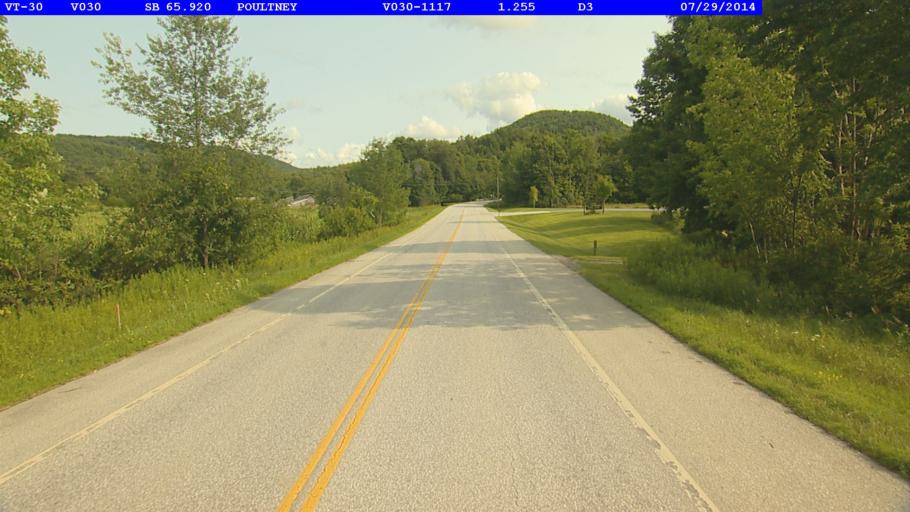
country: US
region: Vermont
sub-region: Rutland County
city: Poultney
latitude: 43.4816
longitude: -73.2020
